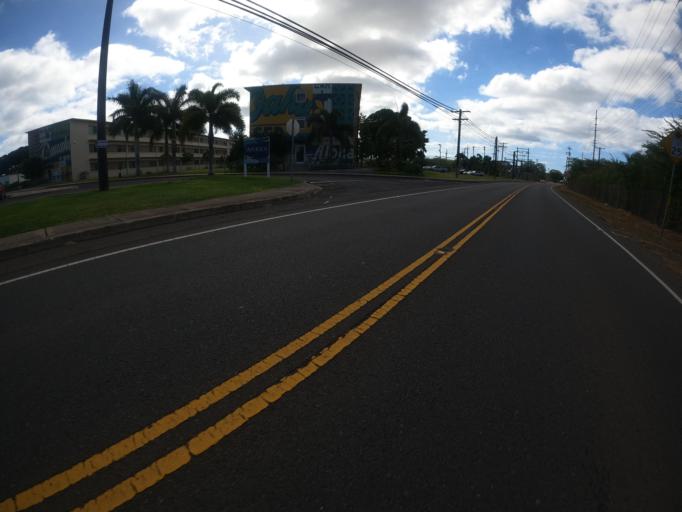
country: US
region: Hawaii
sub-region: Honolulu County
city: Makakilo City
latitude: 21.3229
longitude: -158.0773
